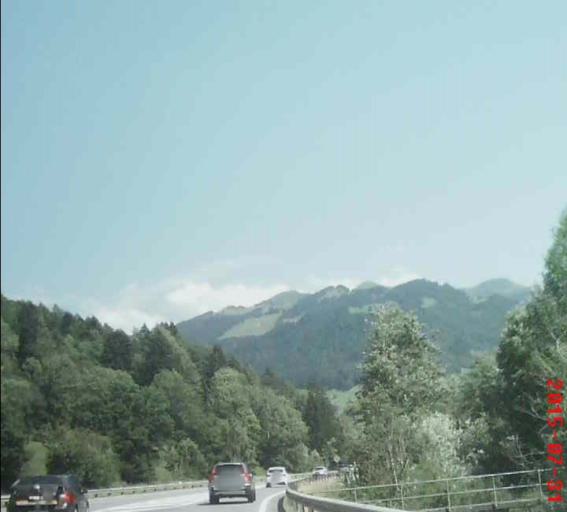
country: CH
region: Grisons
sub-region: Praettigau/Davos District
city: Grusch
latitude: 46.9779
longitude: 9.6552
